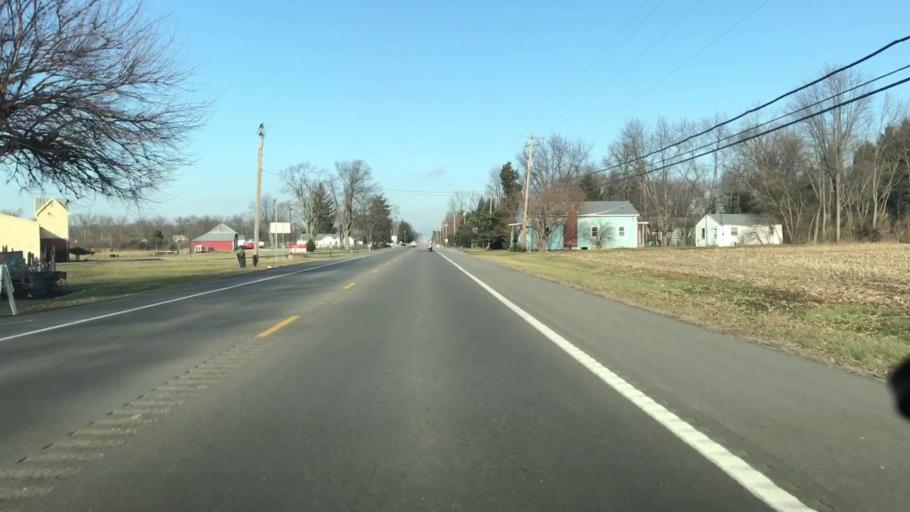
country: US
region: Ohio
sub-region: Greene County
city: Yellow Springs
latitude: 39.8356
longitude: -83.8664
